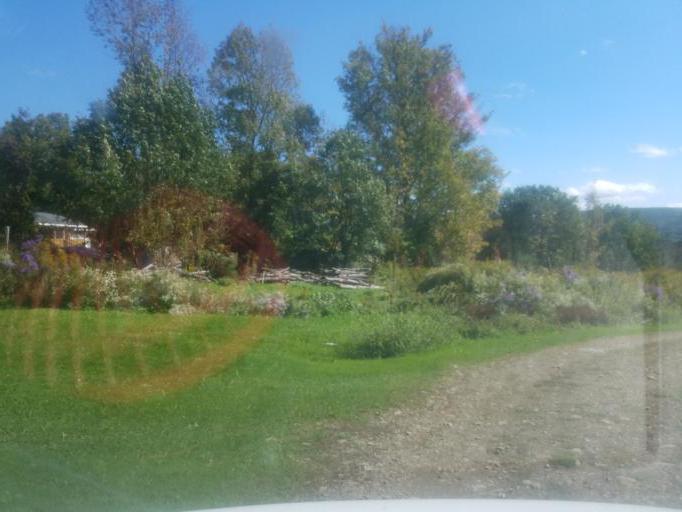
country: US
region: New York
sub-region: Allegany County
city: Friendship
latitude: 42.2761
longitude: -78.1514
